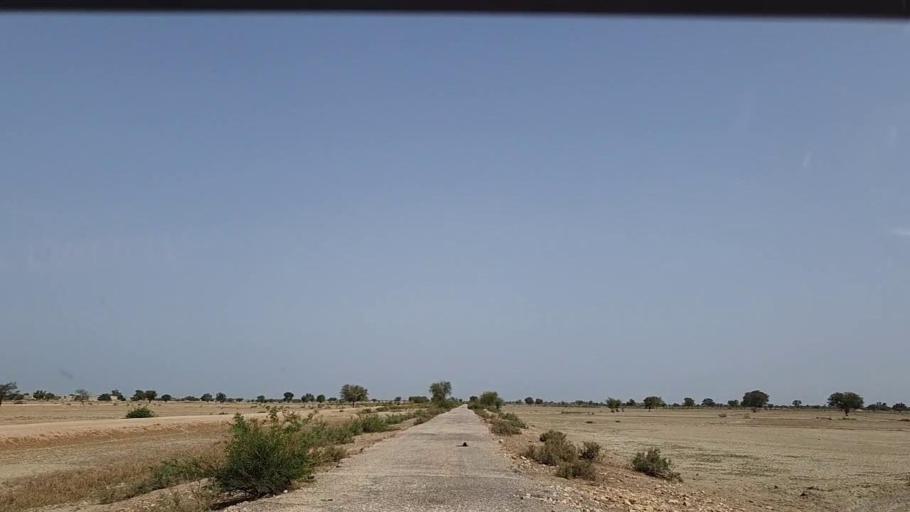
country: PK
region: Sindh
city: Johi
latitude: 26.7547
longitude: 67.6681
